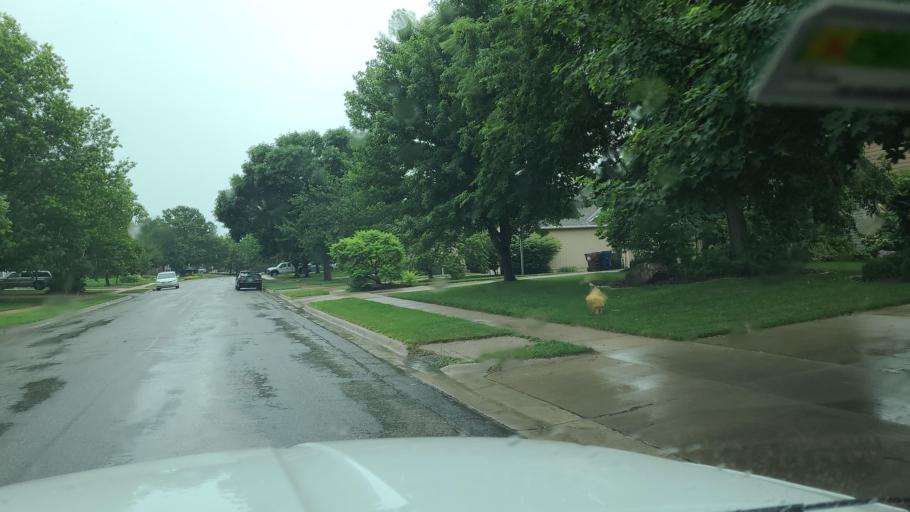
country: US
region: Kansas
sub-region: Douglas County
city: Lawrence
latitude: 38.9675
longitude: -95.3007
